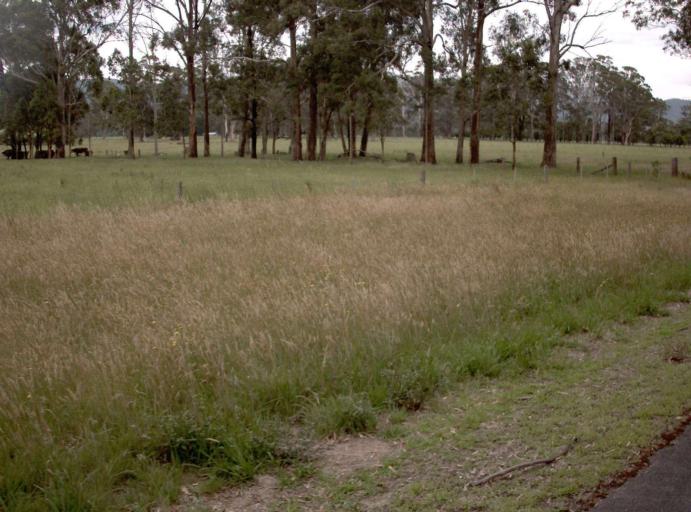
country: AU
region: New South Wales
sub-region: Bombala
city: Bombala
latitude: -37.5215
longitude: 149.1671
